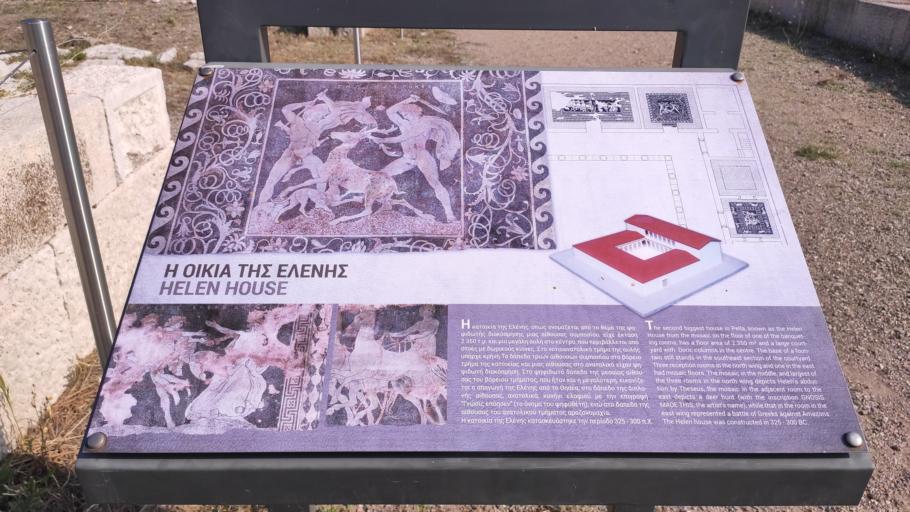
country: GR
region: Central Macedonia
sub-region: Nomos Pellis
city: Pella
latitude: 40.7545
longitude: 22.5180
